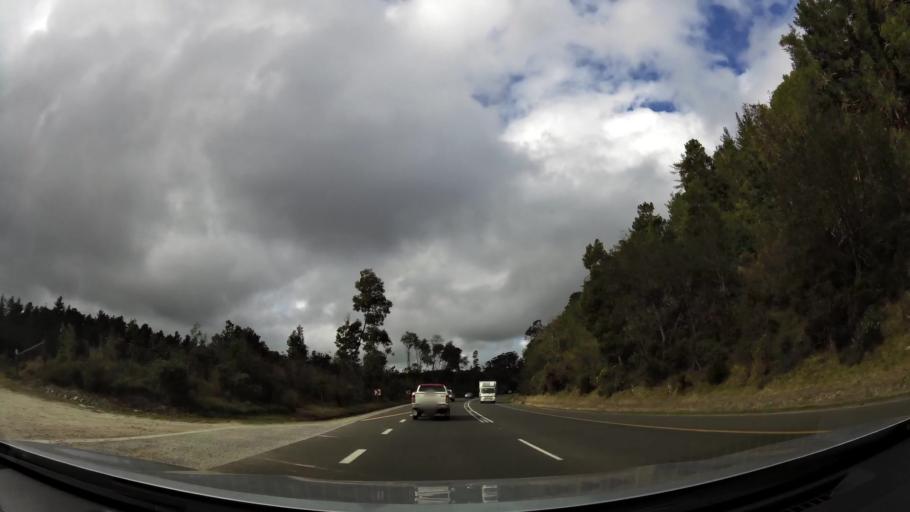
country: ZA
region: Western Cape
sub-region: Eden District Municipality
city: Knysna
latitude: -34.0326
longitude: 23.1922
